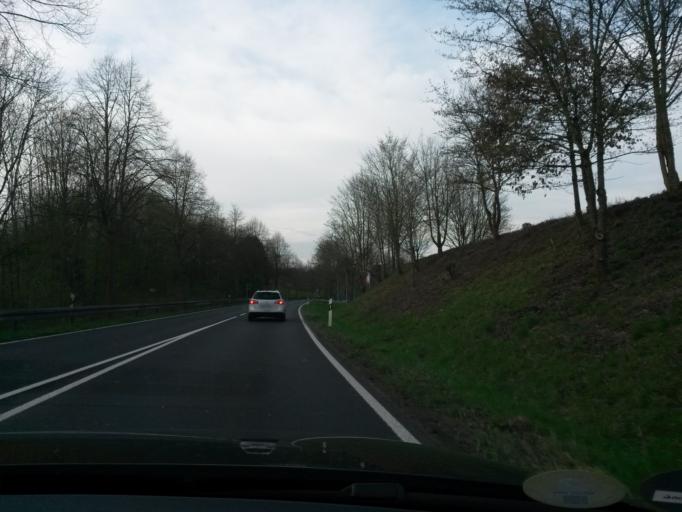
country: DE
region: North Rhine-Westphalia
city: Lohmar
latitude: 50.8859
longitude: 7.2480
